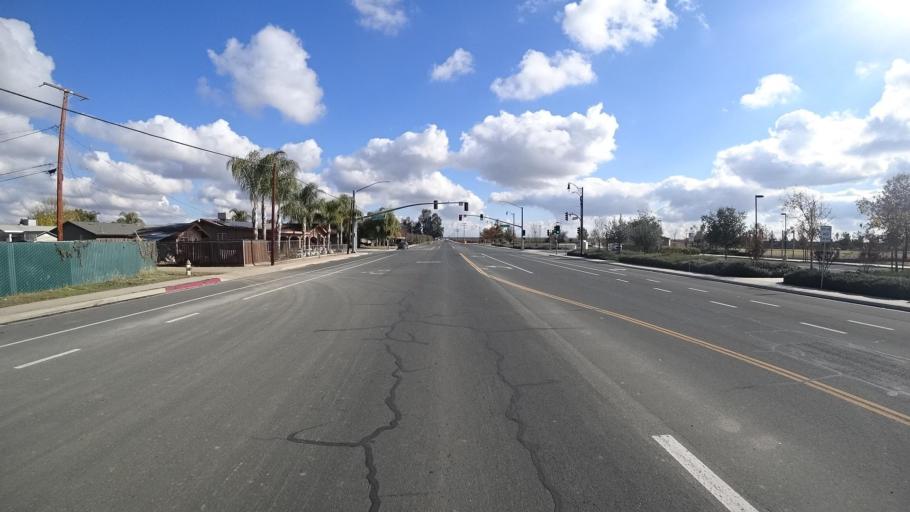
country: US
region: California
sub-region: Kern County
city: McFarland
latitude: 35.6744
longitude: -119.2192
